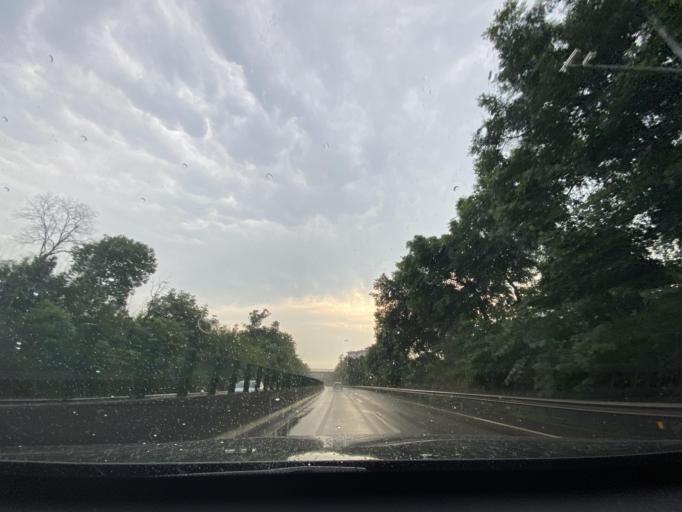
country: CN
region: Sichuan
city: Chonglong
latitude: 29.7694
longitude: 104.7702
